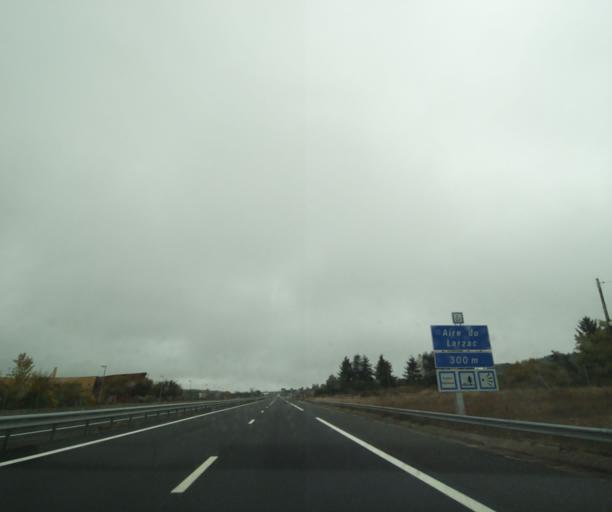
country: FR
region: Midi-Pyrenees
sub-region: Departement de l'Aveyron
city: La Cavalerie
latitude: 43.9854
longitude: 3.1818
